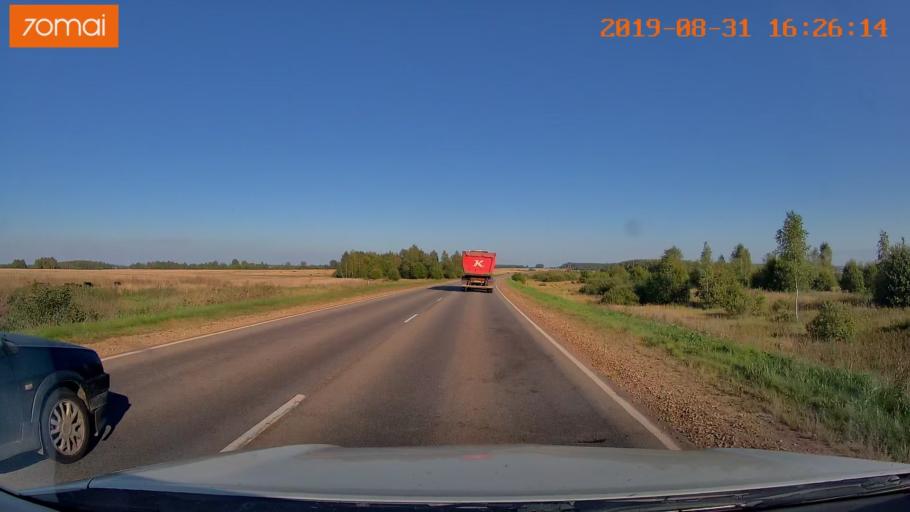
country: RU
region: Kaluga
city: Babynino
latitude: 54.5184
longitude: 35.7300
